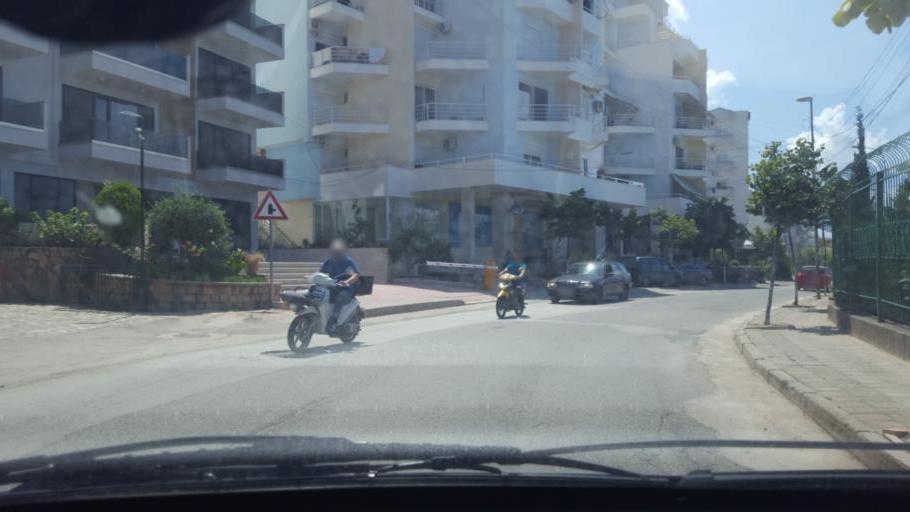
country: AL
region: Vlore
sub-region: Rrethi i Sarandes
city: Sarande
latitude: 39.8599
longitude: 20.0204
